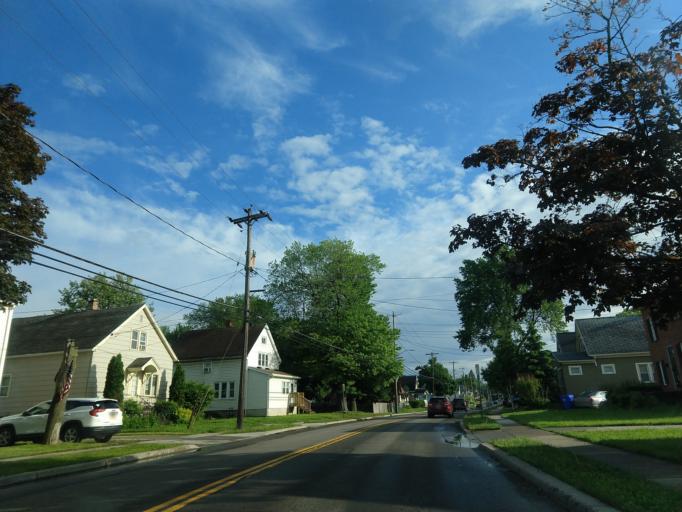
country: US
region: New York
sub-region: Erie County
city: West Seneca
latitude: 42.8473
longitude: -78.7882
